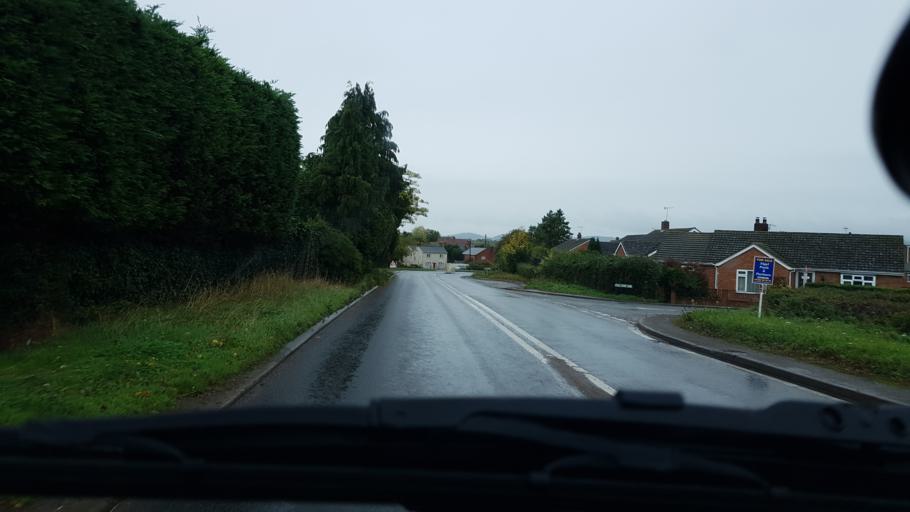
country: GB
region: England
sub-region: Worcestershire
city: Upton upon Severn
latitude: 52.0681
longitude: -2.2030
